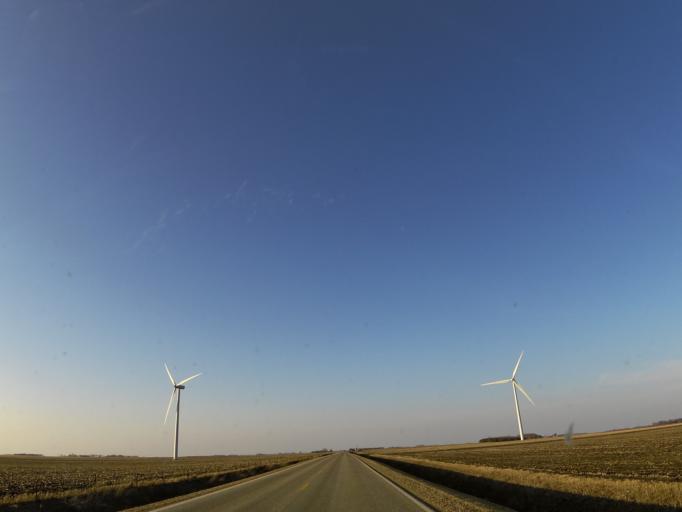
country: US
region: Iowa
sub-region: Worth County
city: Northwood
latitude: 43.4168
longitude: -93.1243
